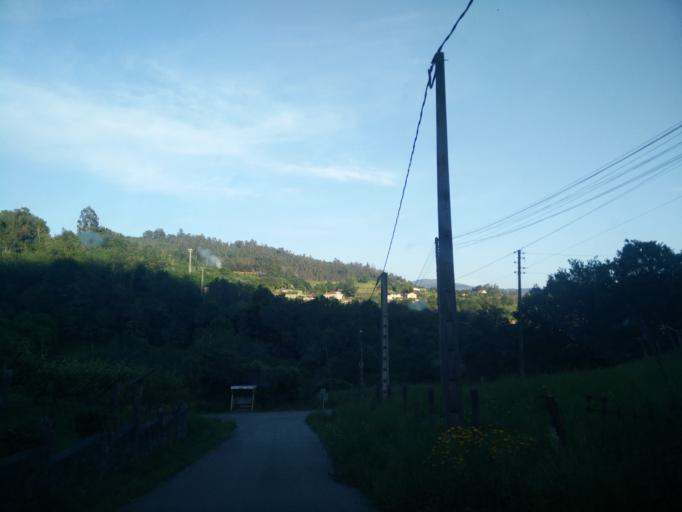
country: ES
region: Galicia
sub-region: Provincia de Pontevedra
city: Mondariz
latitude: 42.2704
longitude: -8.4074
